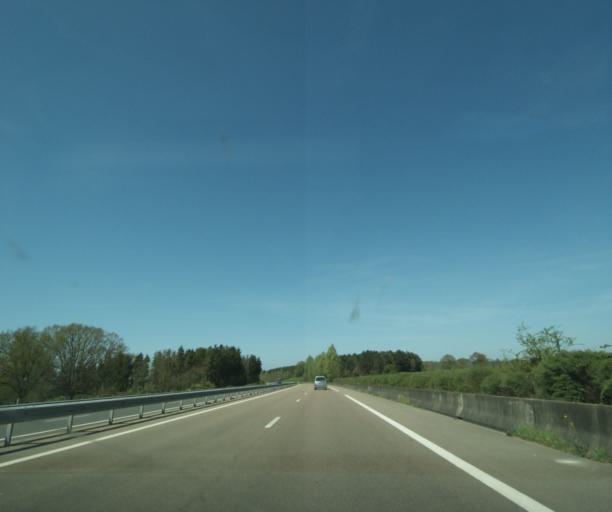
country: FR
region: Bourgogne
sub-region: Departement de la Nievre
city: Pougues-les-Eaux
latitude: 47.0898
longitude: 3.1014
